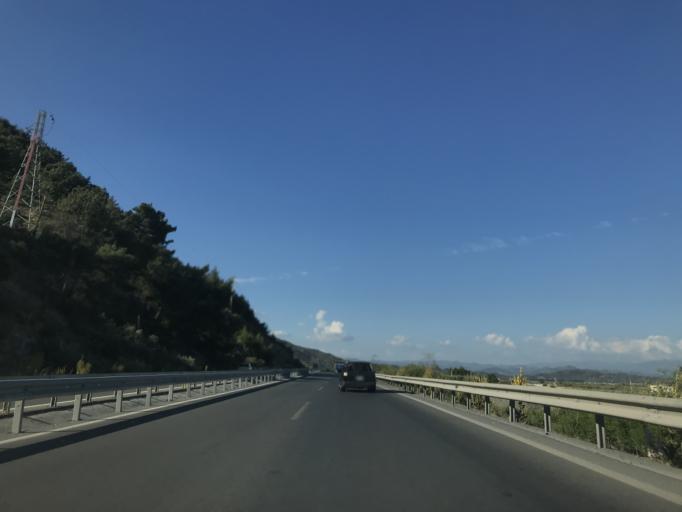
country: TR
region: Aydin
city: Ortaklar
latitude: 37.8049
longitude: 27.4773
